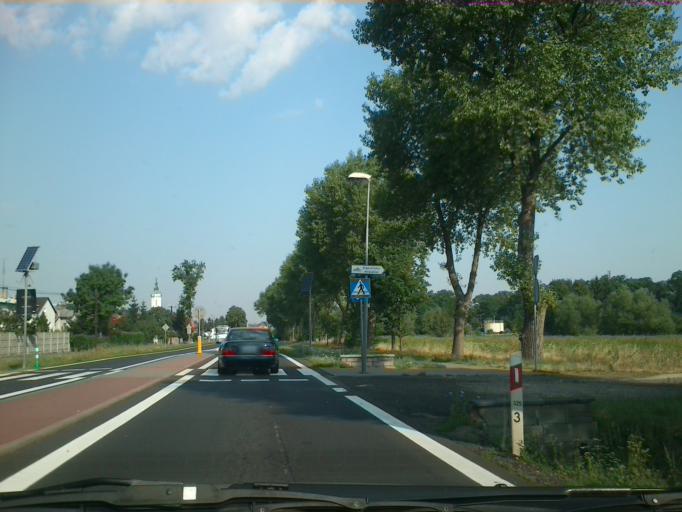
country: PL
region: Lubusz
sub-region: Powiat nowosolski
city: Nowe Miasteczko
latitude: 51.6881
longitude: 15.7410
